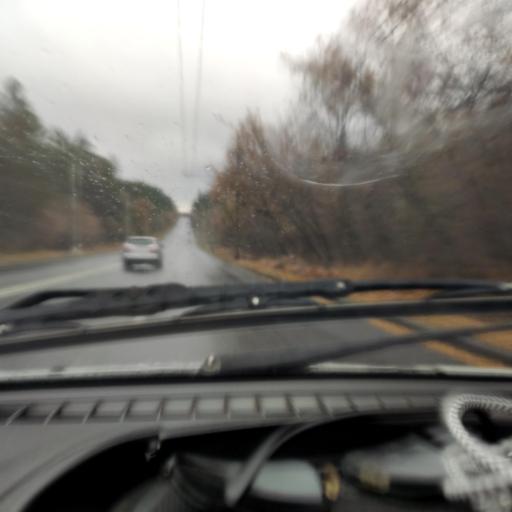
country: RU
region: Samara
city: Zhigulevsk
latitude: 53.5015
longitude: 49.4634
